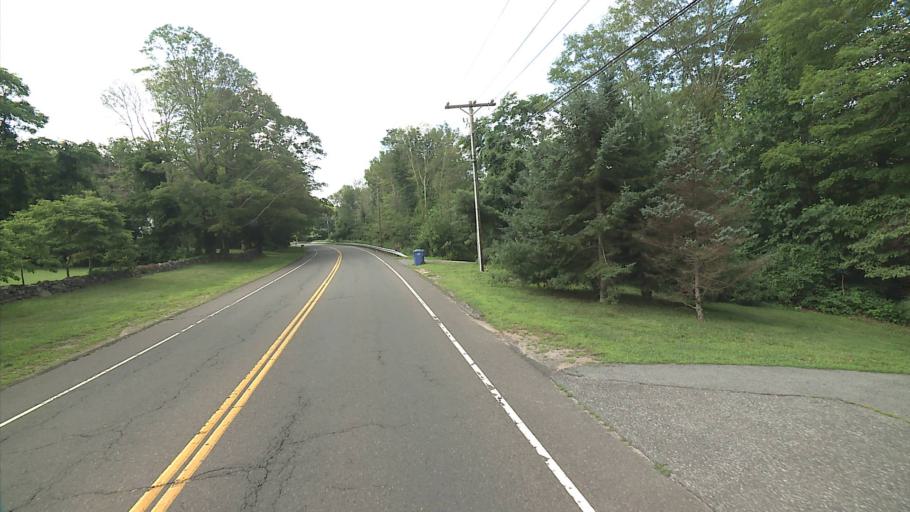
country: US
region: Connecticut
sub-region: Middlesex County
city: Clinton
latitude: 41.3227
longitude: -72.4941
